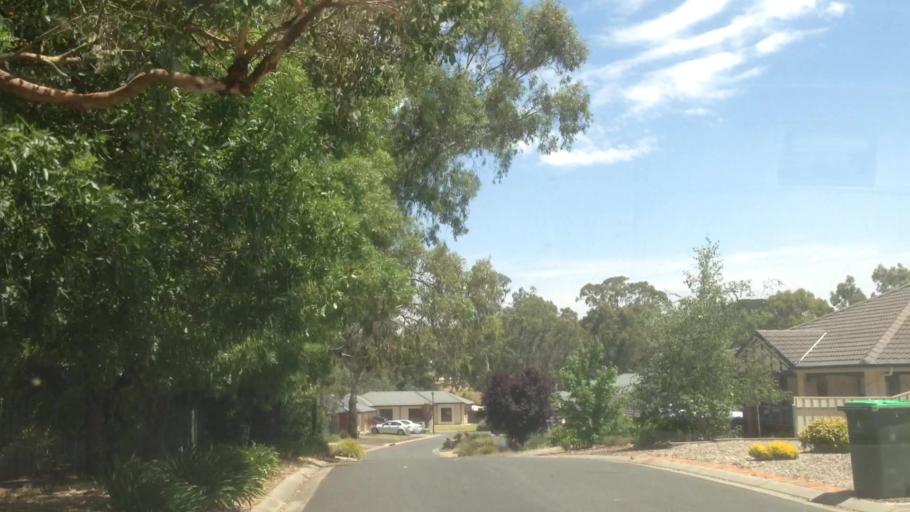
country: AU
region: South Australia
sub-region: Adelaide Hills
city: Birdwood
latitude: -34.8168
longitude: 138.9707
